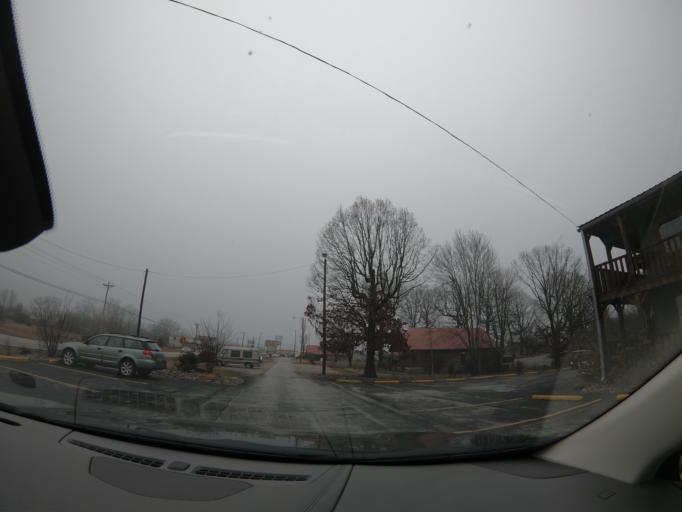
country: US
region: Tennessee
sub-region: Marion County
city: Monteagle
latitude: 35.2366
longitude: -85.8522
